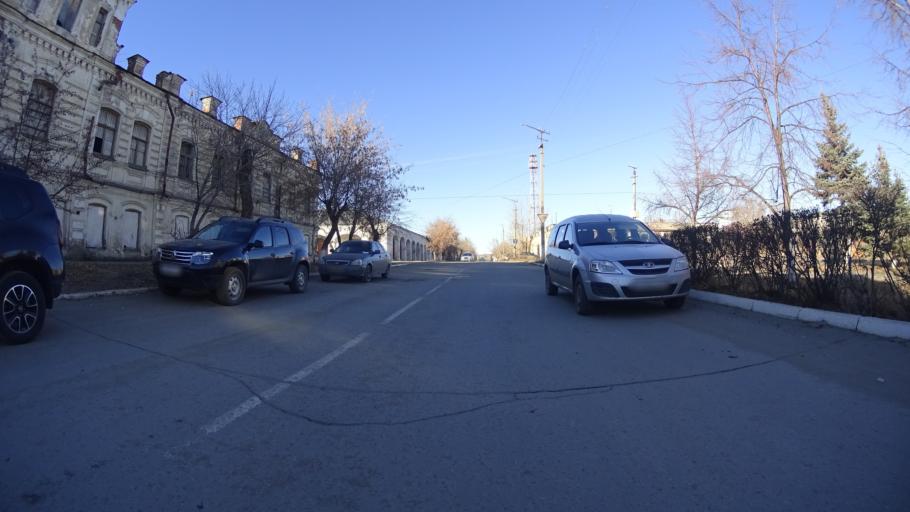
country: RU
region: Chelyabinsk
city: Troitsk
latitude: 54.0810
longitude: 61.5618
